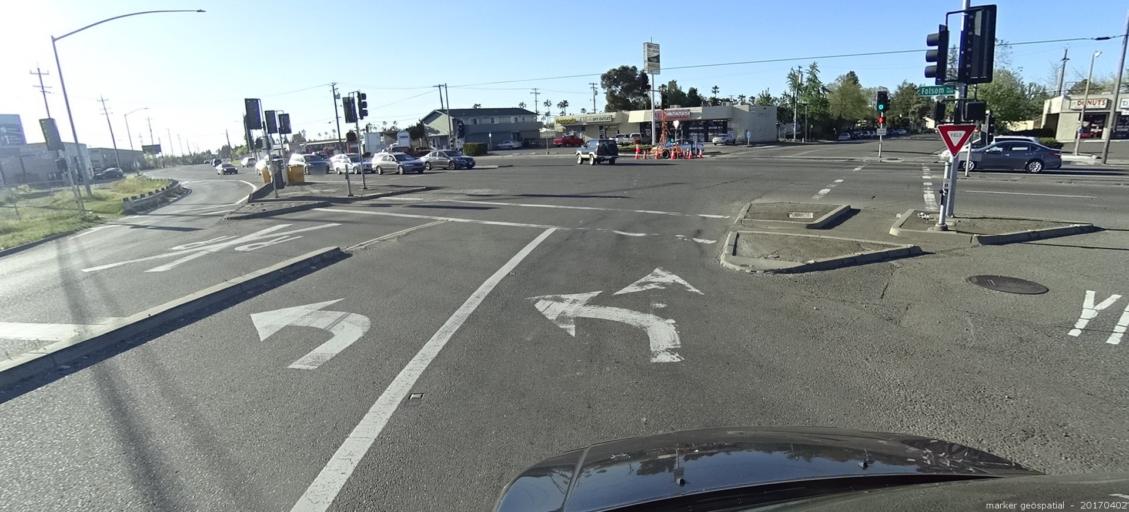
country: US
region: California
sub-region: Sacramento County
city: Rosemont
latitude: 38.5468
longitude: -121.3988
